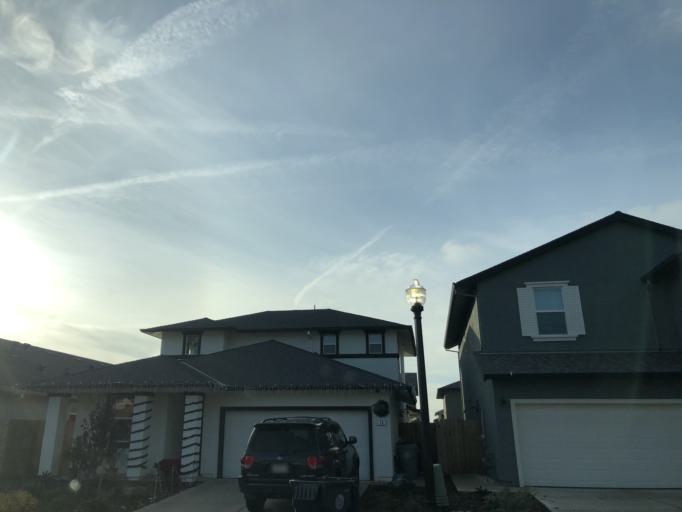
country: US
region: California
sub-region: Sacramento County
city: Parkway
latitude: 38.5501
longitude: -121.4410
